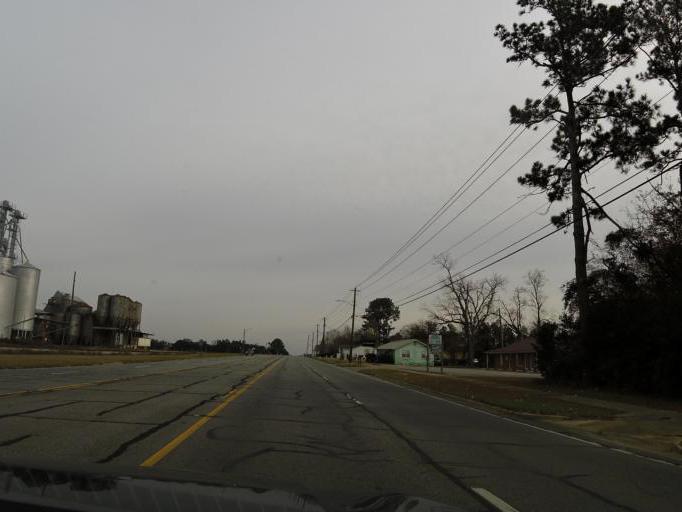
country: US
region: Georgia
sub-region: Seminole County
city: Donalsonville
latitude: 31.0360
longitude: -84.8654
